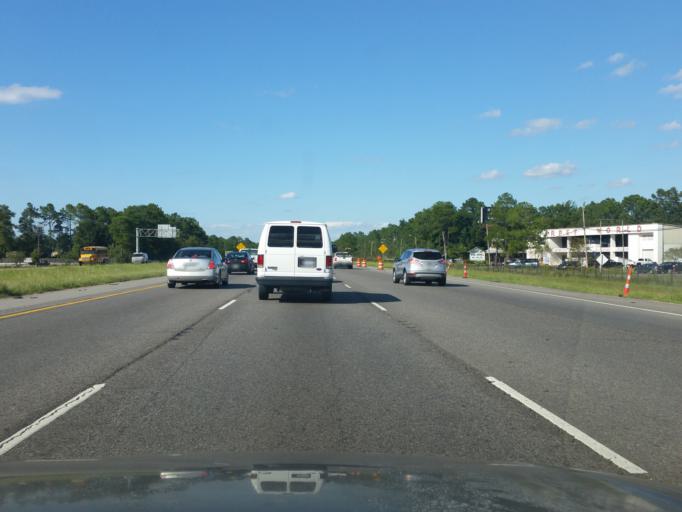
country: US
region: Louisiana
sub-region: Saint Tammany Parish
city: Slidell
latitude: 30.2893
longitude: -89.7478
